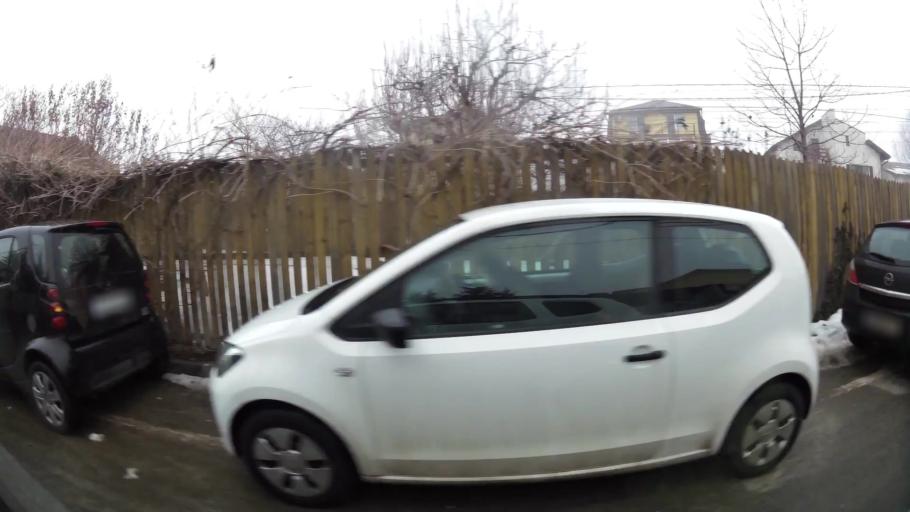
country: RO
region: Ilfov
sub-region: Comuna Chiajna
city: Rosu
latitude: 44.4559
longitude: 25.9940
